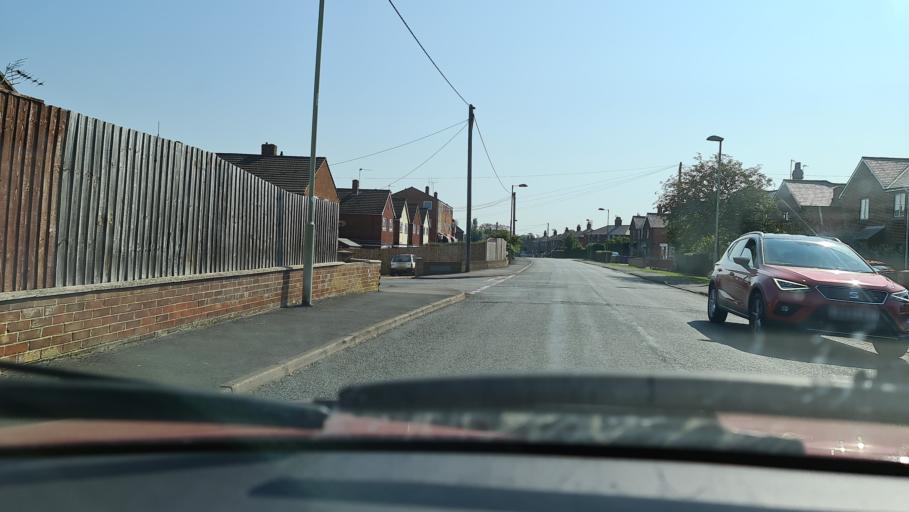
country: GB
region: England
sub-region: Oxfordshire
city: Bicester
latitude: 51.9056
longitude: -1.1612
